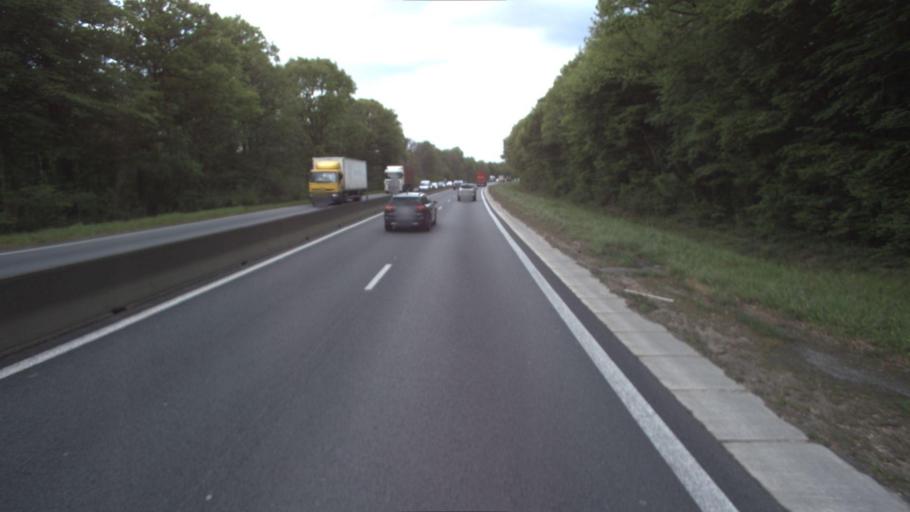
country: FR
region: Ile-de-France
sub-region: Departement de Seine-et-Marne
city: Gretz-Armainvilliers
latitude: 48.7333
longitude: 2.7207
